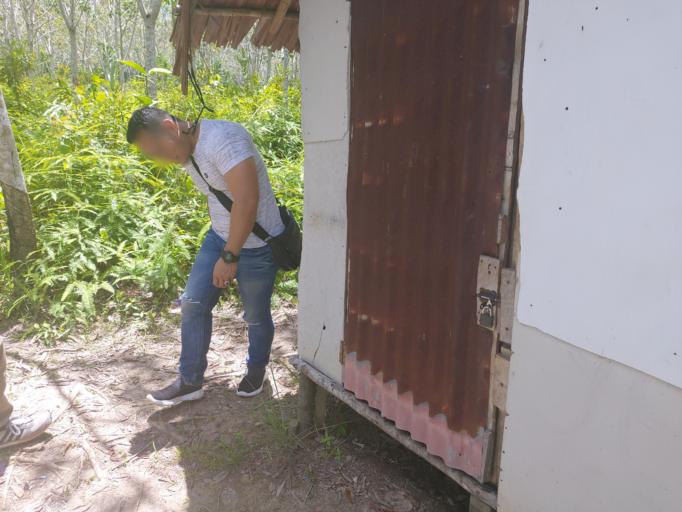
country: ID
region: Central Kalimantan
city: Tamianglayang
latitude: -2.0005
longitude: 115.2056
